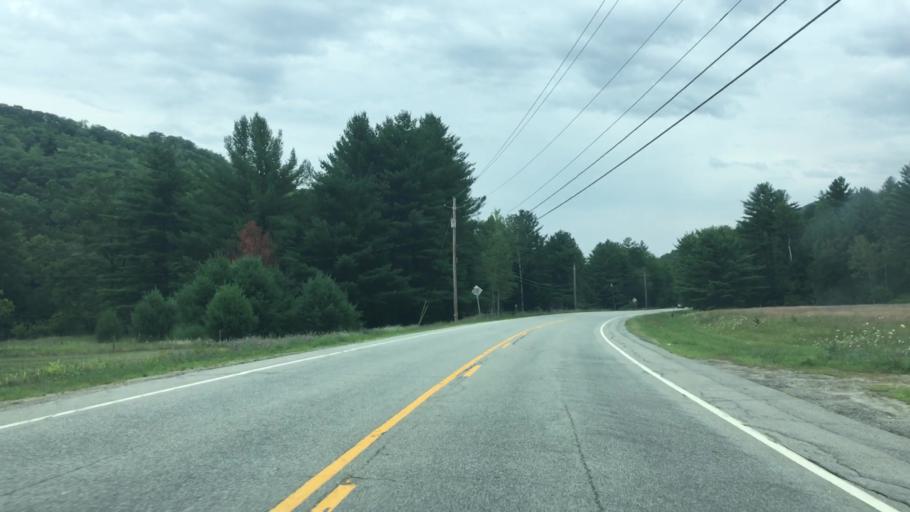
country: US
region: New York
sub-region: Essex County
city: Lake Placid
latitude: 44.2625
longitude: -73.7930
